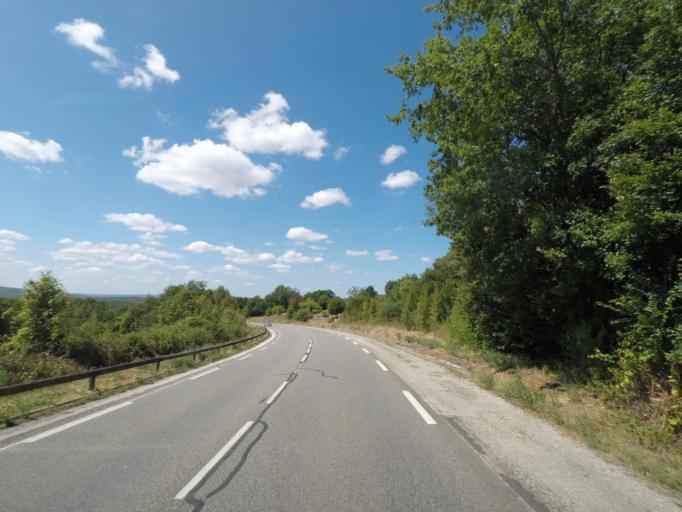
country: FR
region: Midi-Pyrenees
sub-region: Departement du Lot
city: Figeac
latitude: 44.6226
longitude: 1.9329
